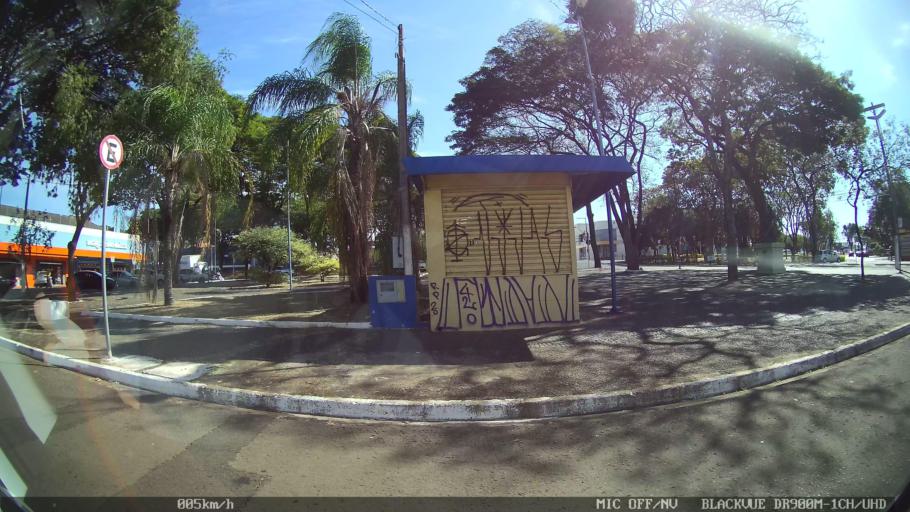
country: BR
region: Sao Paulo
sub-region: Franca
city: Franca
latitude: -20.5353
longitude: -47.4125
